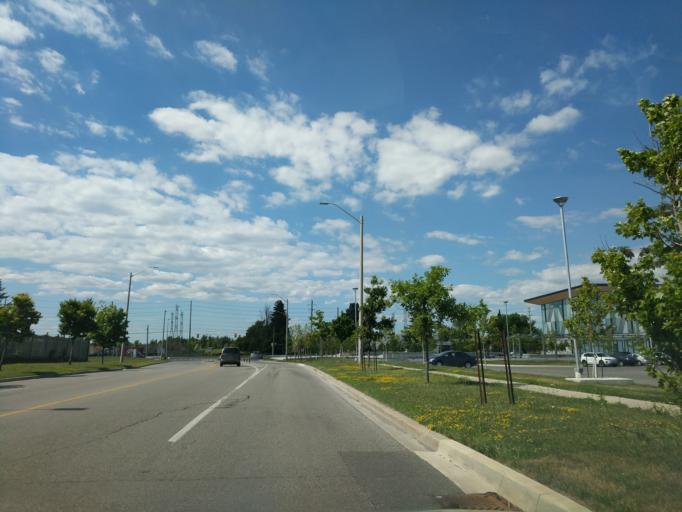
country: CA
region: Ontario
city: Markham
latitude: 43.8509
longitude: -79.2674
